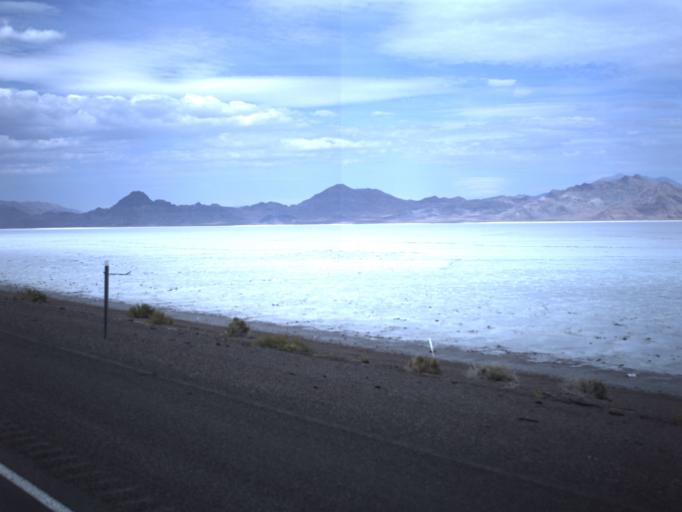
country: US
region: Utah
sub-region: Tooele County
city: Wendover
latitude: 40.7390
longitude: -113.8314
